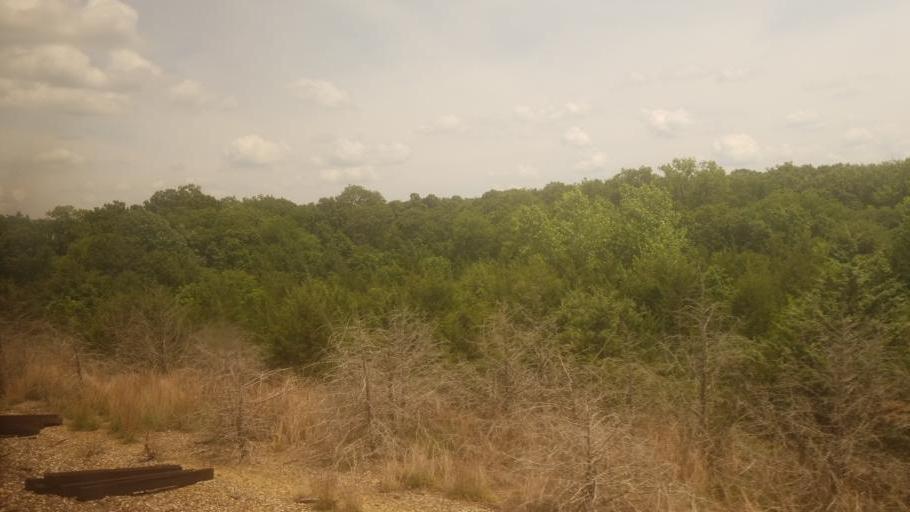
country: US
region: Missouri
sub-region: Clark County
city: Kahoka
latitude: 40.4830
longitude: -91.6948
